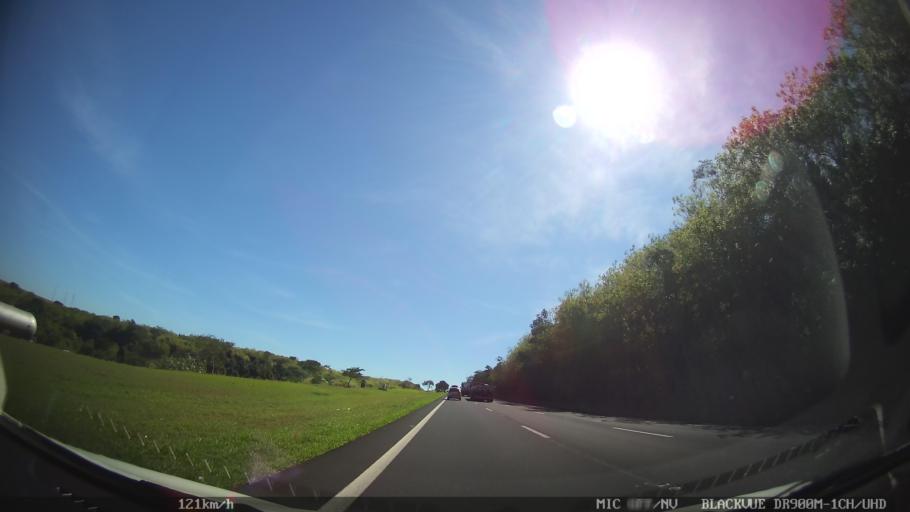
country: BR
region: Sao Paulo
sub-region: Santa Rita Do Passa Quatro
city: Santa Rita do Passa Quatro
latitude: -21.7067
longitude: -47.5936
